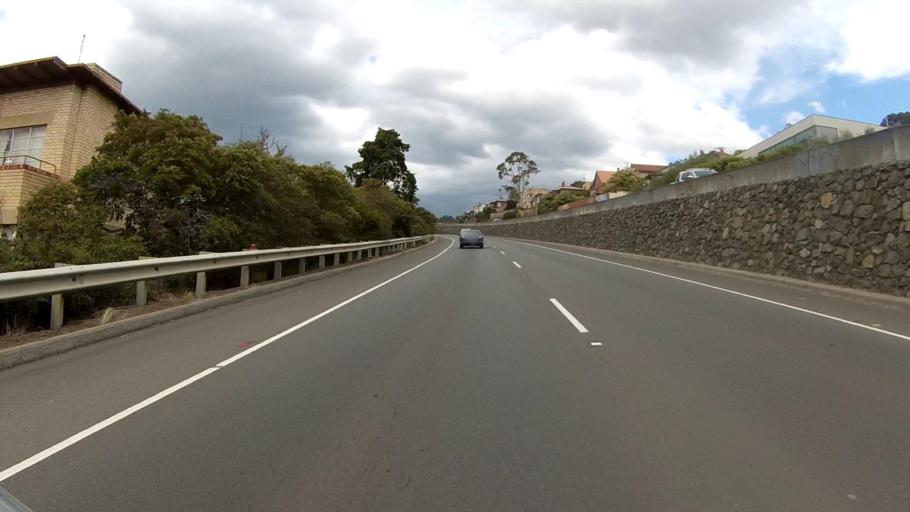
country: AU
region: Tasmania
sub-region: Hobart
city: Dynnyrne
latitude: -42.9011
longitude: 147.3159
